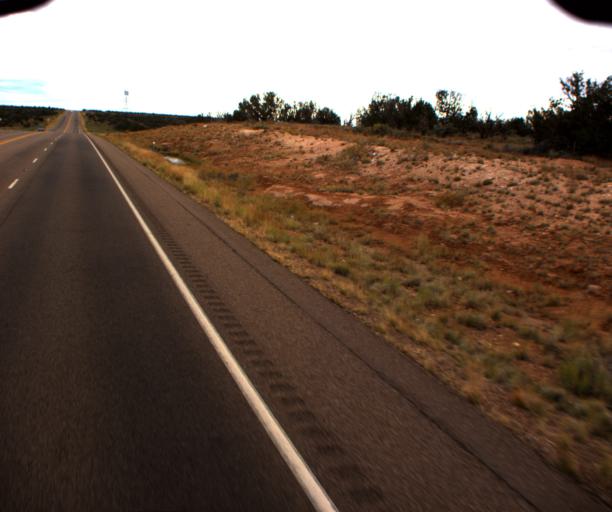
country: US
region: Arizona
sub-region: Navajo County
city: Snowflake
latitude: 34.6436
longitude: -110.0967
